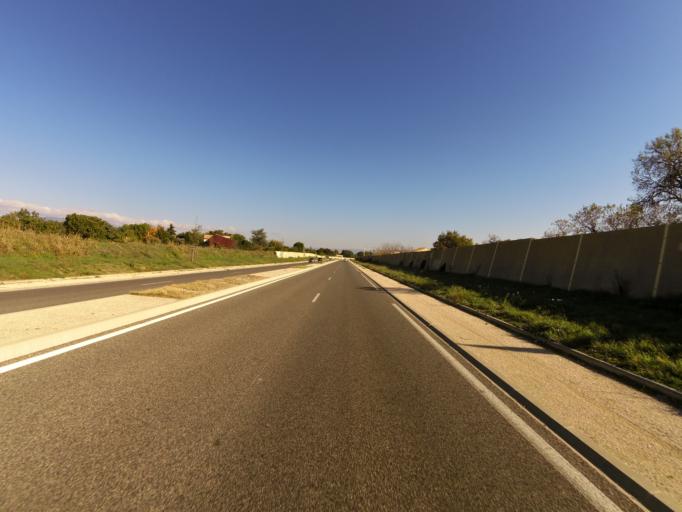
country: FR
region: Provence-Alpes-Cote d'Azur
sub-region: Departement du Vaucluse
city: Carpentras
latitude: 44.0679
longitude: 5.0597
